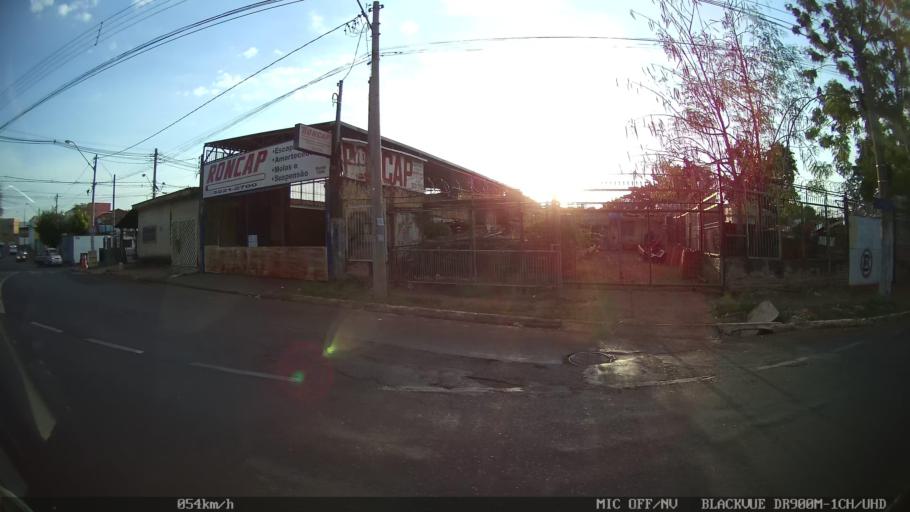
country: BR
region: Sao Paulo
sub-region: Ribeirao Preto
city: Ribeirao Preto
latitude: -21.1519
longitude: -47.8092
